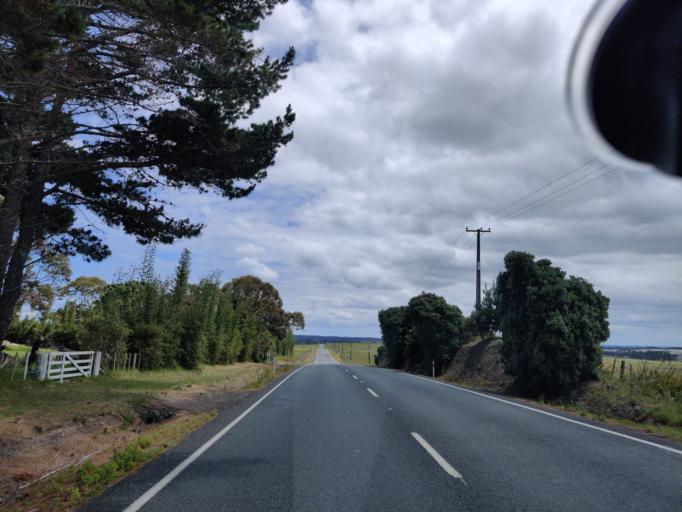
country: NZ
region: Northland
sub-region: Far North District
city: Kaitaia
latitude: -34.6938
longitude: 173.0227
